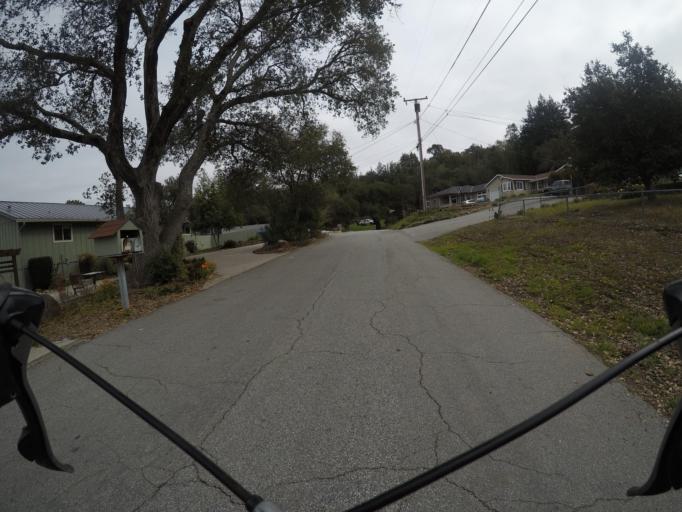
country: US
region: California
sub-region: Santa Cruz County
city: Scotts Valley
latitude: 37.0616
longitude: -121.9948
